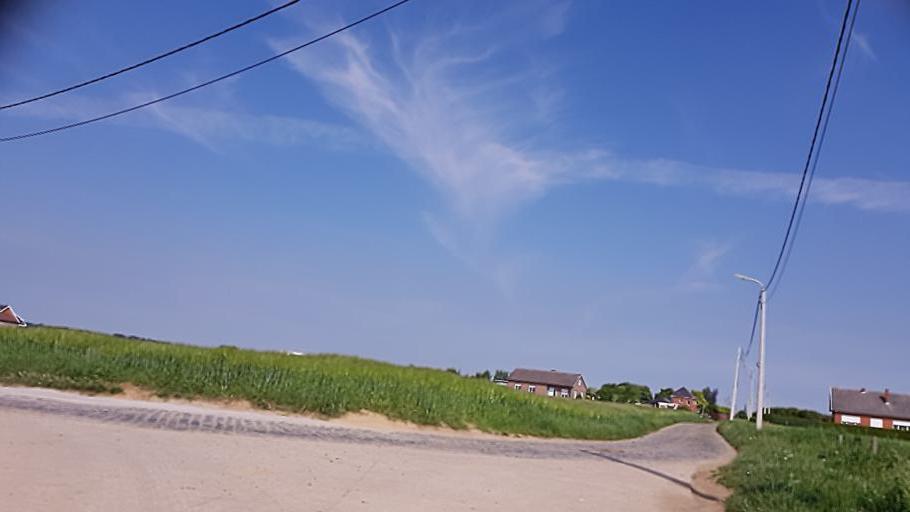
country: BE
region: Flanders
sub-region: Provincie Vlaams-Brabant
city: Huldenberg
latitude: 50.8034
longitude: 4.5652
